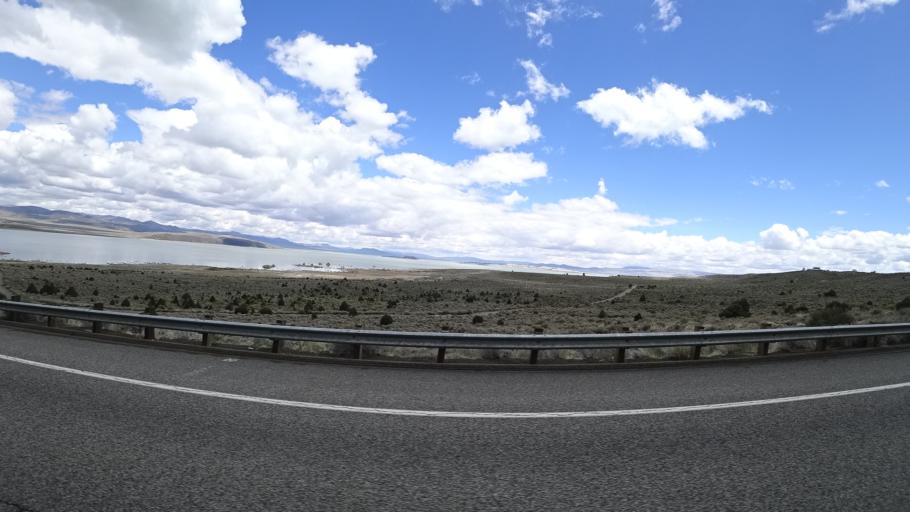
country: US
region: California
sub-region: Mono County
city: Bridgeport
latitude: 37.9708
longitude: -119.1324
